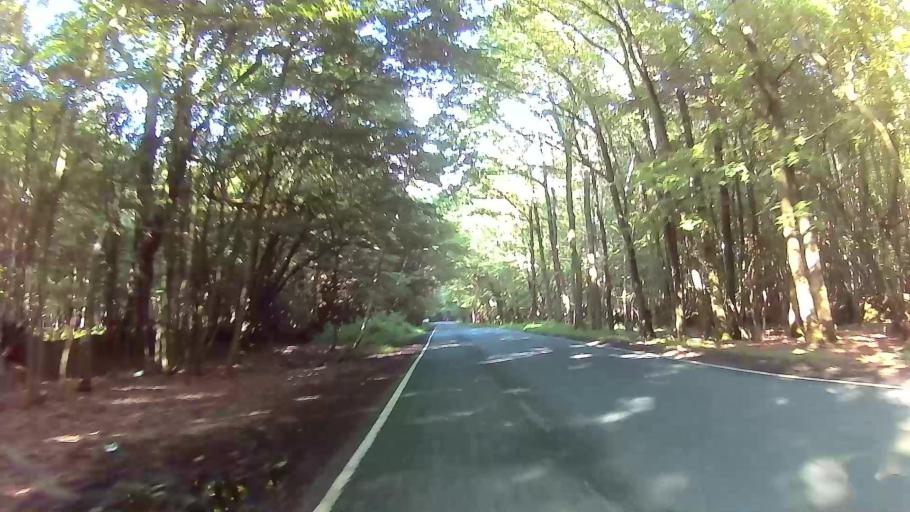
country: GB
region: England
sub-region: Essex
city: Ingatestone
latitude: 51.6974
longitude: 0.3478
